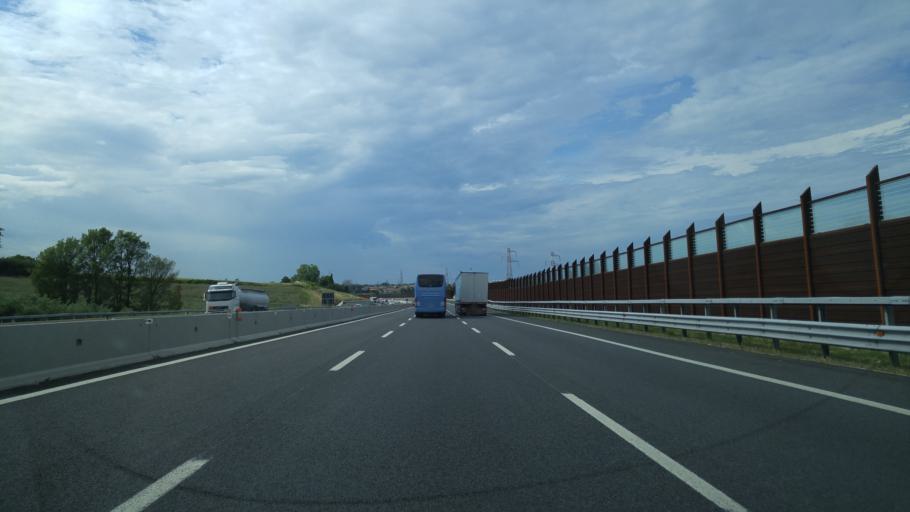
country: IT
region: Emilia-Romagna
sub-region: Provincia di Rimini
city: Rivazzurra
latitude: 44.0216
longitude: 12.5840
